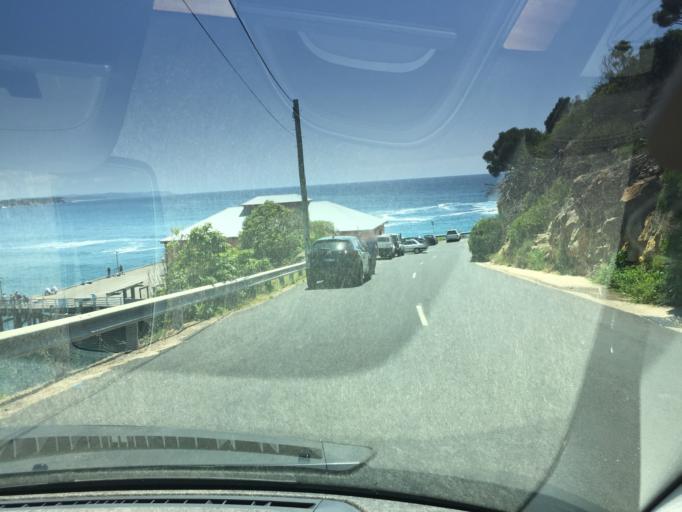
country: AU
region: New South Wales
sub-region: Bega Valley
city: Bega
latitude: -36.7262
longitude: 149.9883
